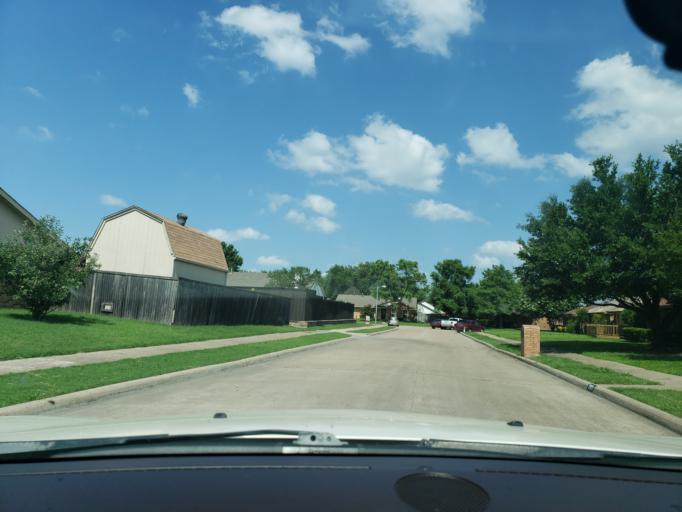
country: US
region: Texas
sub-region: Dallas County
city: Rowlett
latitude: 32.8946
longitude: -96.5760
